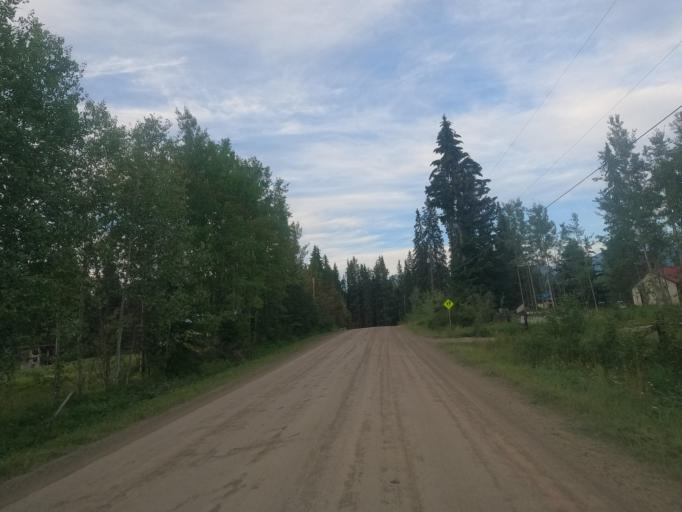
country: CA
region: British Columbia
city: Golden
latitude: 51.4398
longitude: -117.0414
